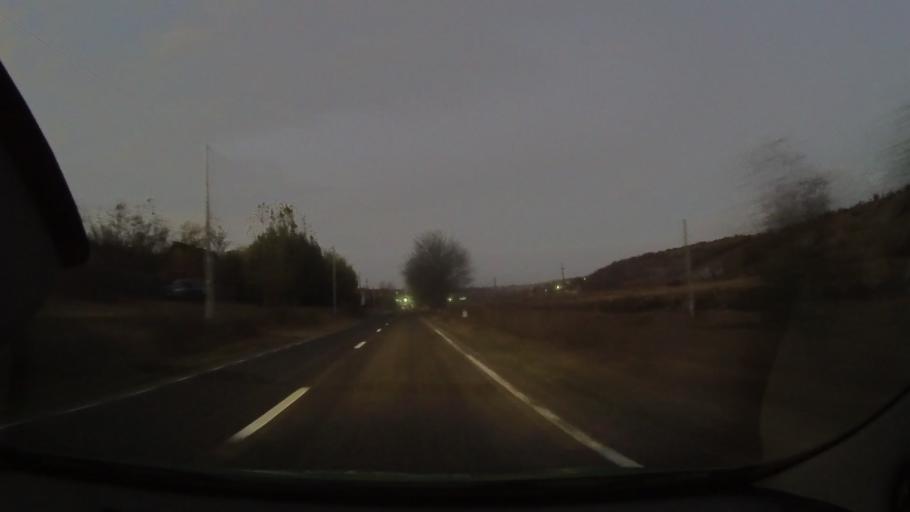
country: RO
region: Constanta
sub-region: Comuna Ion Corvin
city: Ion Corvin
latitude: 44.1055
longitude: 27.8005
